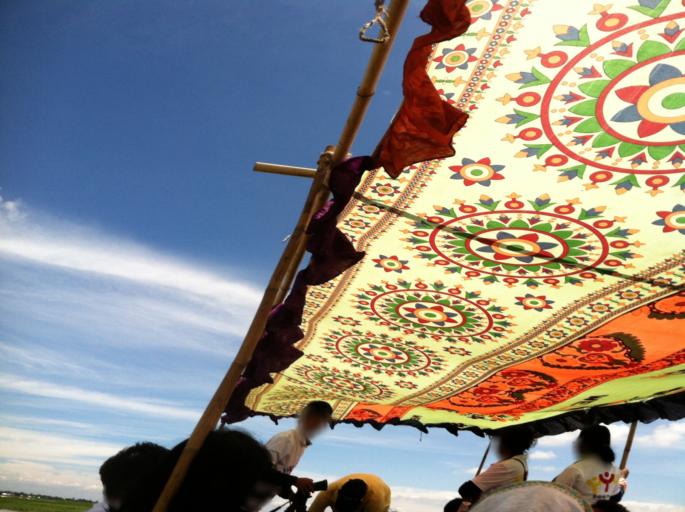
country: BD
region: Sylhet
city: Baniachang
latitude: 24.6412
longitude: 91.3348
